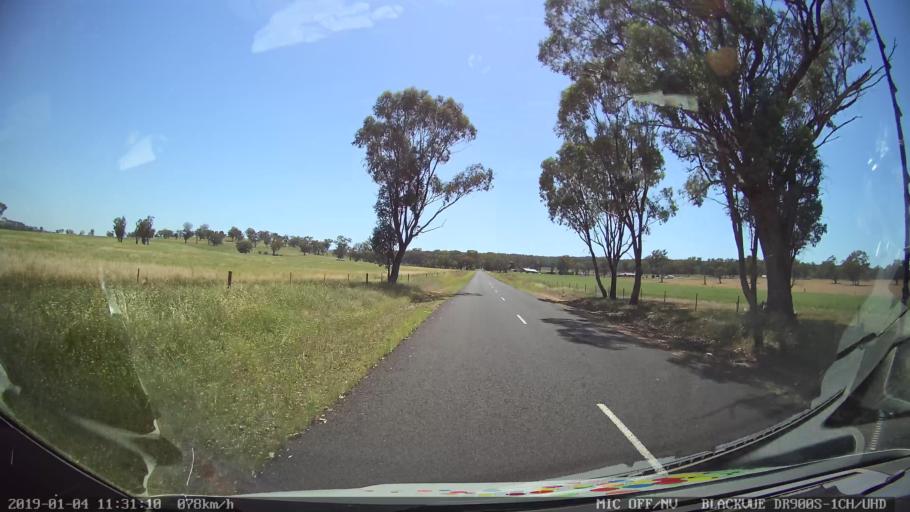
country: AU
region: New South Wales
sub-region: Cabonne
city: Molong
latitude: -33.0736
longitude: 148.7900
